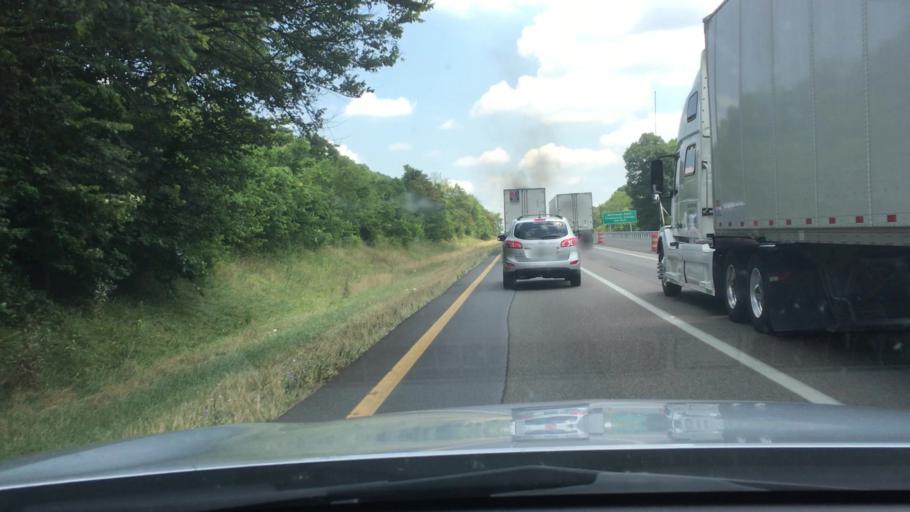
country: US
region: Tennessee
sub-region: Sullivan County
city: Colonial Heights
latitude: 36.4914
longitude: -82.4655
